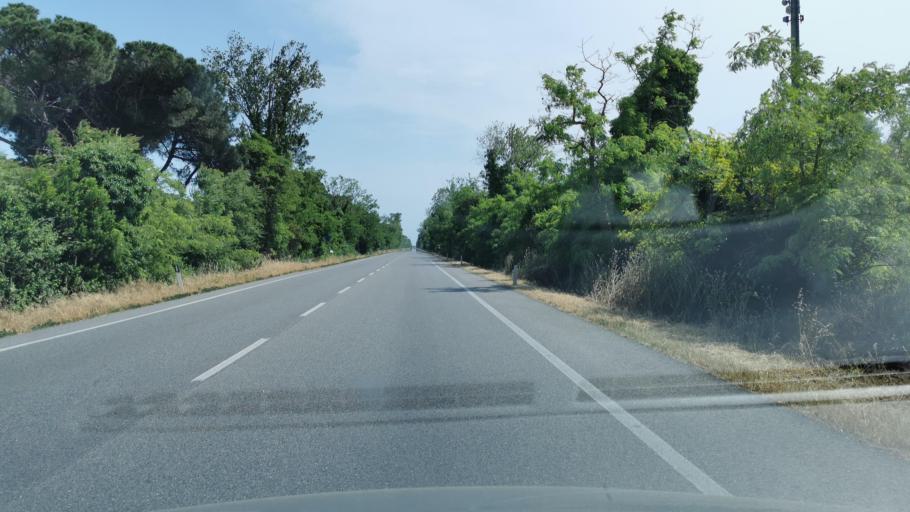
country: IT
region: Emilia-Romagna
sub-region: Provincia di Ferrara
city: Lido degli Estensi
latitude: 44.6040
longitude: 12.2450
